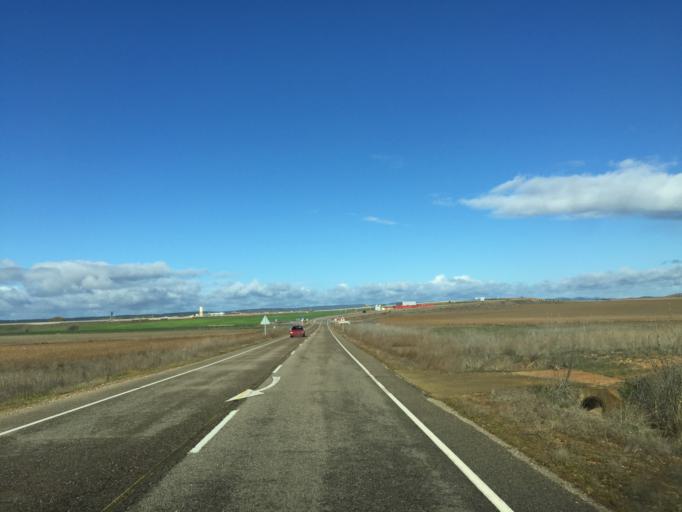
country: ES
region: Castille and Leon
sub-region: Provincia de Zamora
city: Manganeses de la Lampreana
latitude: 41.7602
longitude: -5.7457
